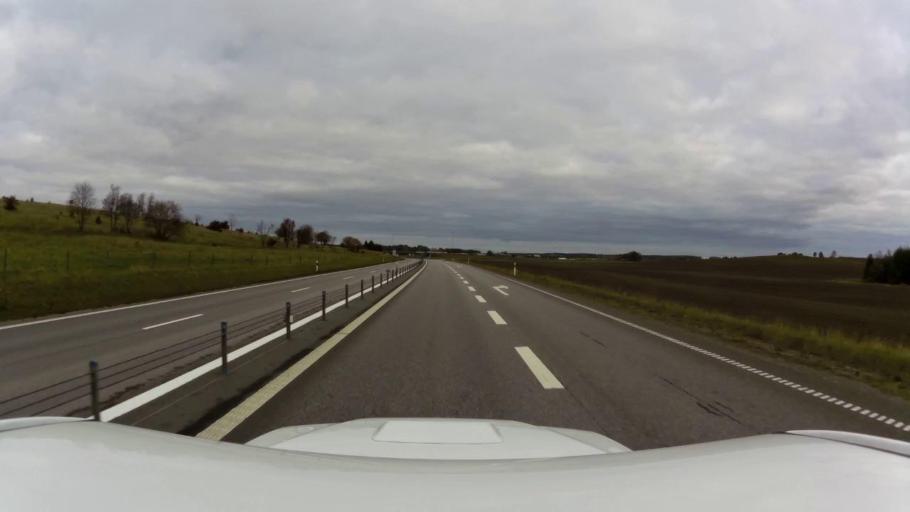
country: SE
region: OEstergoetland
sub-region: Linkopings Kommun
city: Ljungsbro
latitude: 58.4757
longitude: 15.4891
